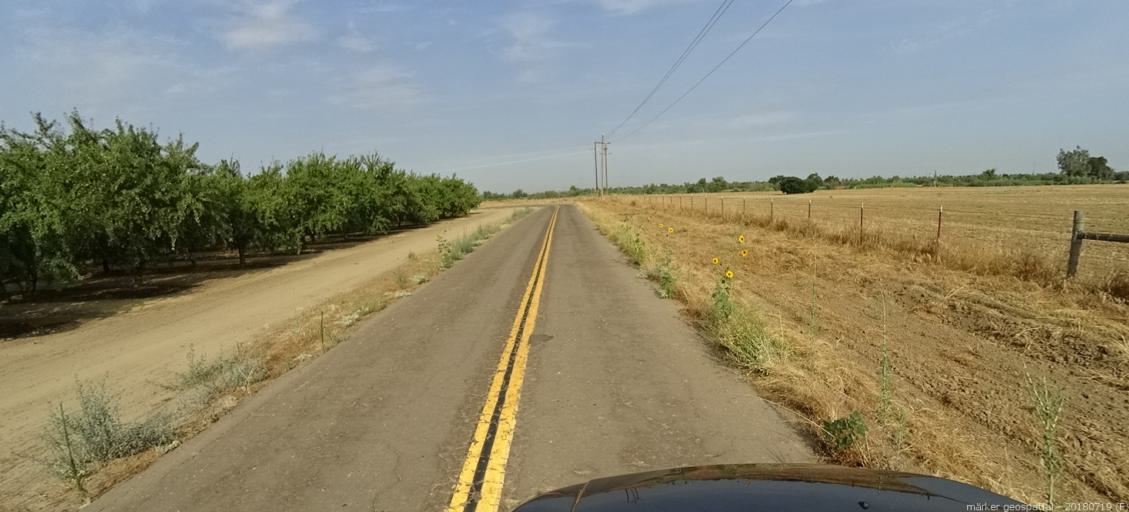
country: US
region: California
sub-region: Madera County
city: Fairmead
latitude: 37.1128
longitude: -120.2100
